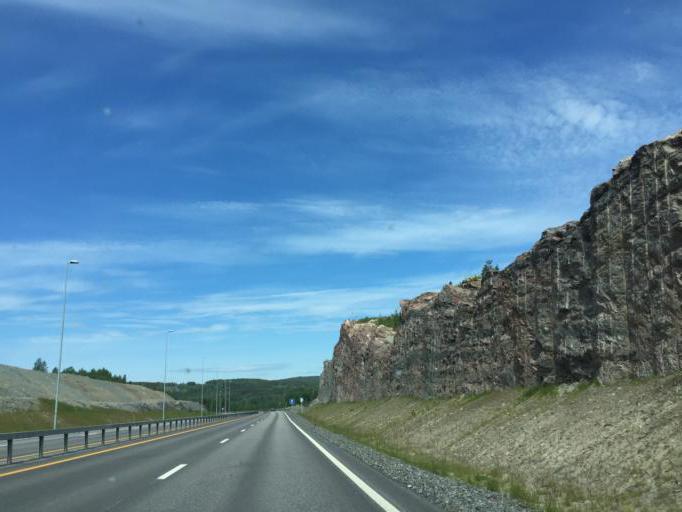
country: NO
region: Hedmark
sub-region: Kongsvinger
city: Kongsvinger
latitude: 60.2035
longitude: 11.9519
